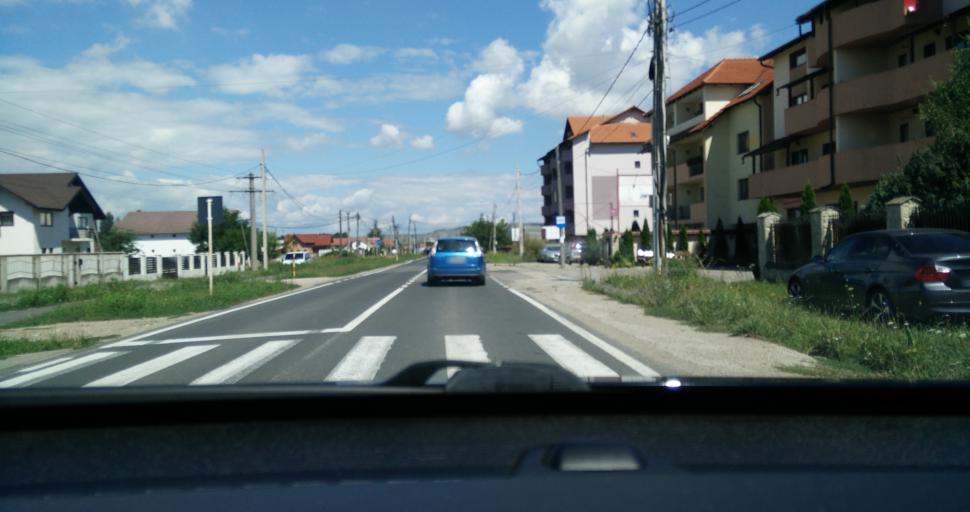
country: RO
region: Alba
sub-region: Municipiul Sebes
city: Petresti
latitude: 45.9370
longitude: 23.5623
